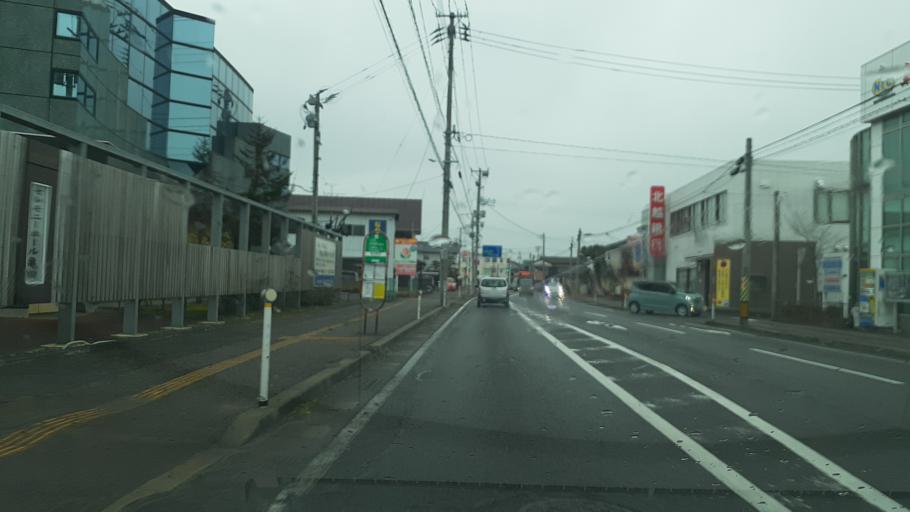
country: JP
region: Niigata
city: Kameda-honcho
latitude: 37.8759
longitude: 139.1063
